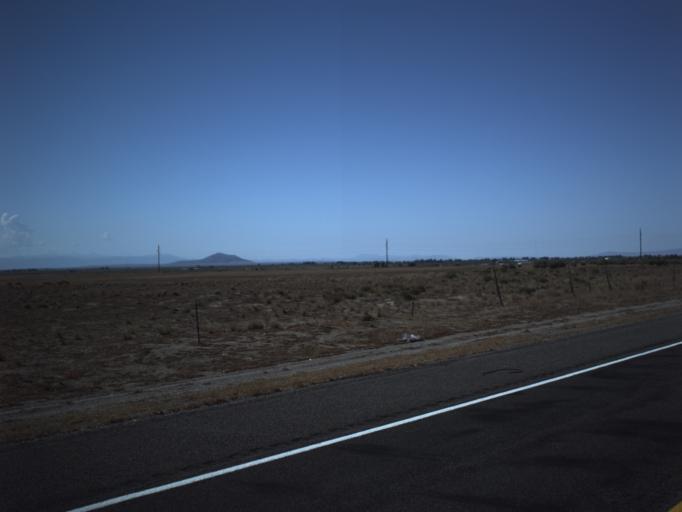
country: US
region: Utah
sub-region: Millard County
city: Delta
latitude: 39.3734
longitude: -112.5362
